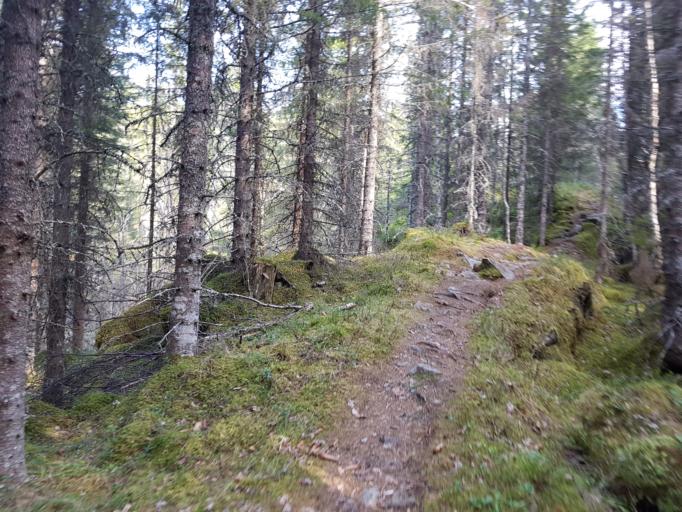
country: NO
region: Sor-Trondelag
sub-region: Trondheim
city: Trondheim
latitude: 63.4403
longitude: 10.2892
